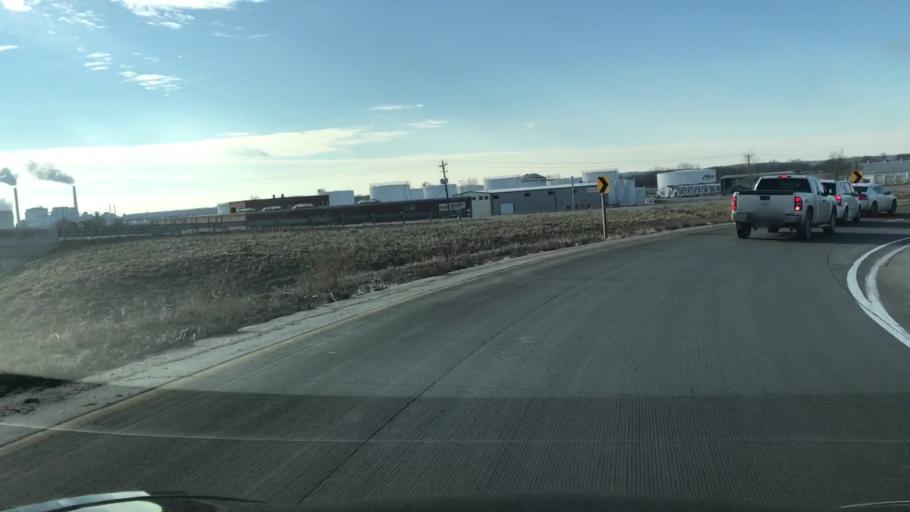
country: US
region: Iowa
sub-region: Pottawattamie County
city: Council Bluffs
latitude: 41.2186
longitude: -95.8315
